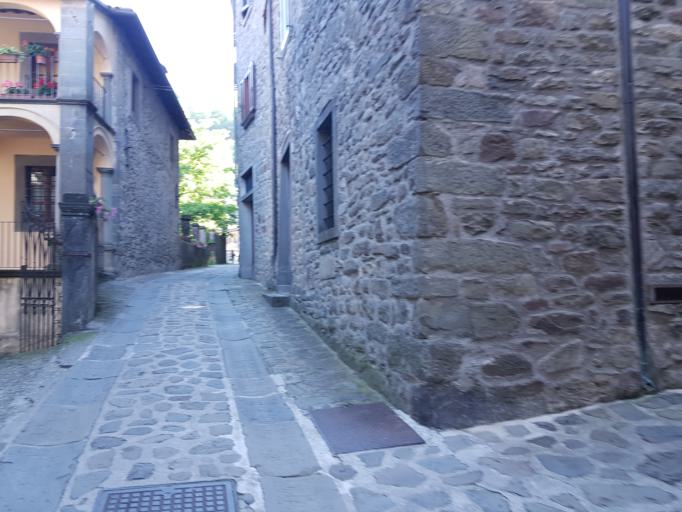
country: IT
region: Tuscany
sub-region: Provincia di Lucca
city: San Romano in Garfagnana
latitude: 44.1696
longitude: 10.3464
